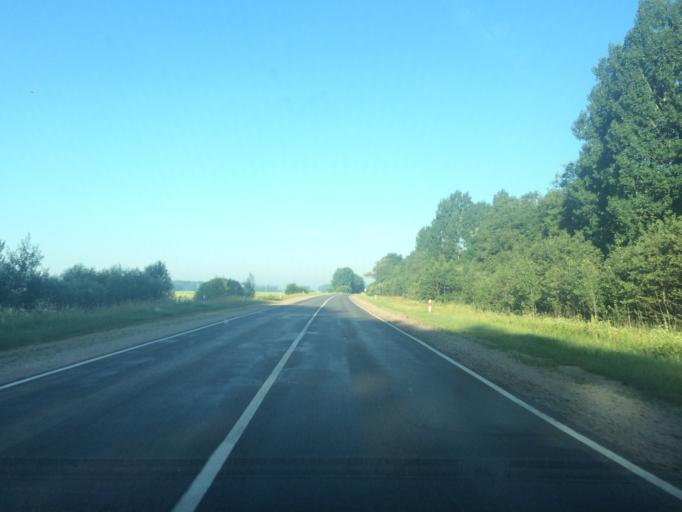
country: LT
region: Utenos apskritis
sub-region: Anyksciai
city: Anyksciai
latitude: 55.3669
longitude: 25.0053
